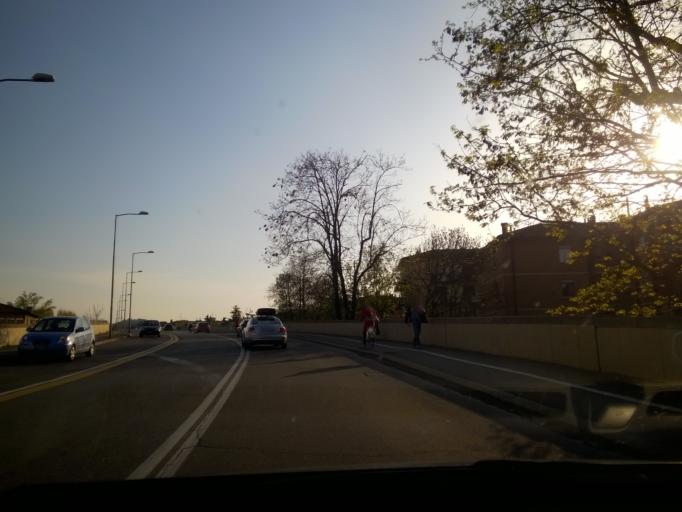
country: IT
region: Emilia-Romagna
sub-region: Provincia di Bologna
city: Bologna
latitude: 44.5021
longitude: 11.3615
